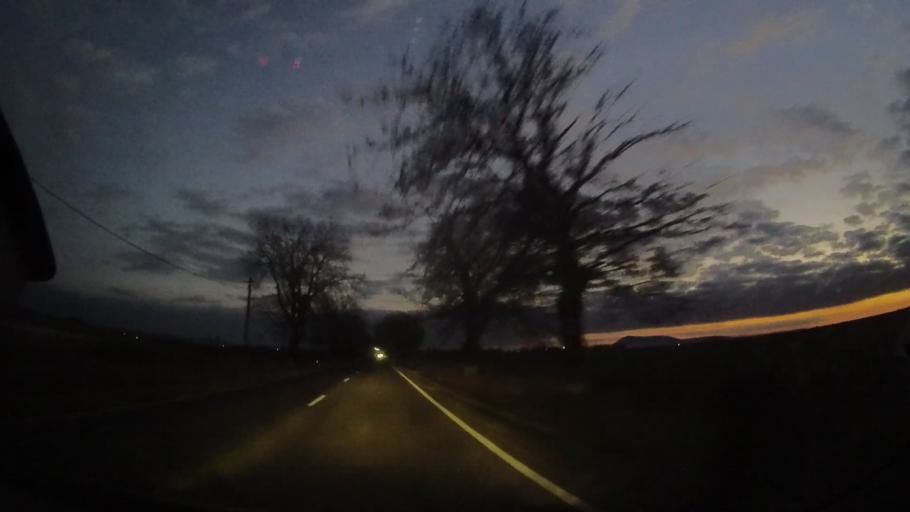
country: RO
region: Tulcea
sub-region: Comuna Mihail Kogalniceanu
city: Mihail Kogalniceanu
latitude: 45.0503
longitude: 28.7364
